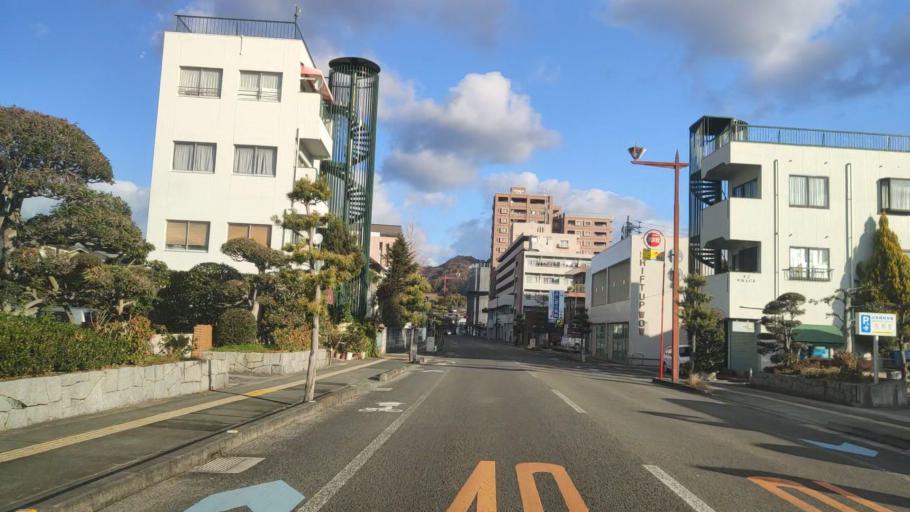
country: JP
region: Ehime
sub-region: Shikoku-chuo Shi
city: Matsuyama
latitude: 33.8503
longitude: 132.7808
